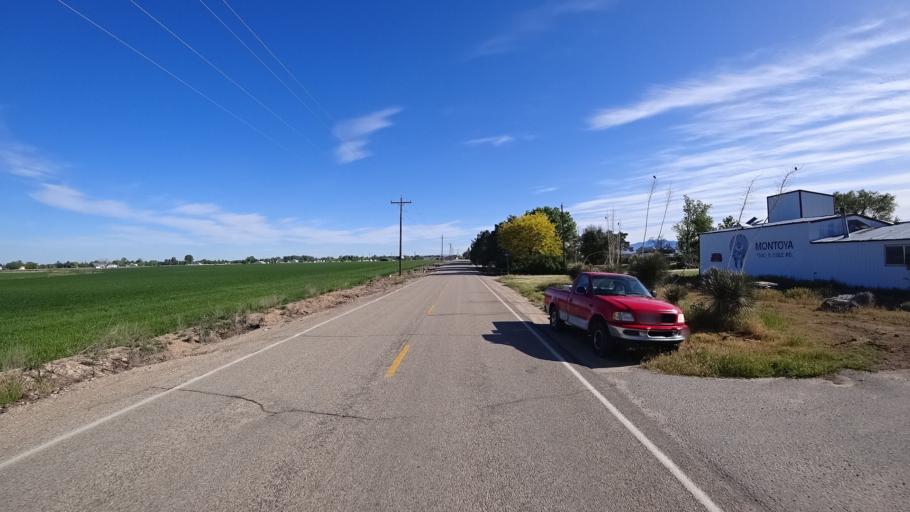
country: US
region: Idaho
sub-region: Ada County
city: Garden City
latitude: 43.5338
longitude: -116.2748
